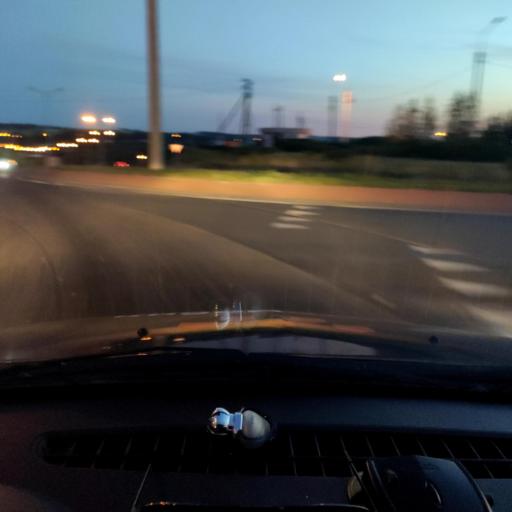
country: RU
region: Belgorod
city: Gubkin
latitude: 51.2609
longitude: 37.5326
